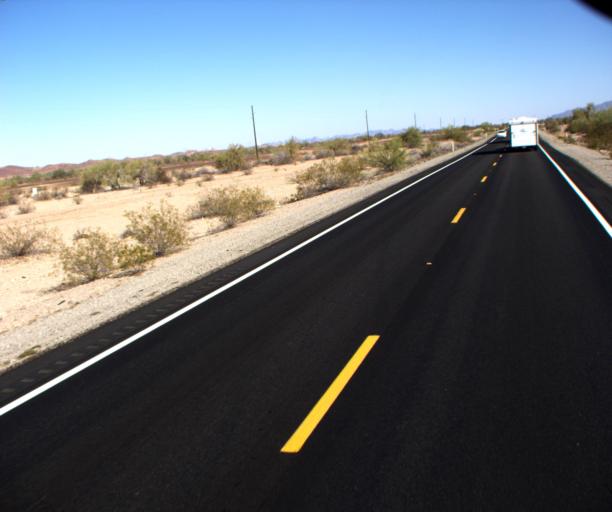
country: US
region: Arizona
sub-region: Yuma County
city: Wellton
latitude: 32.9877
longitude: -114.2880
